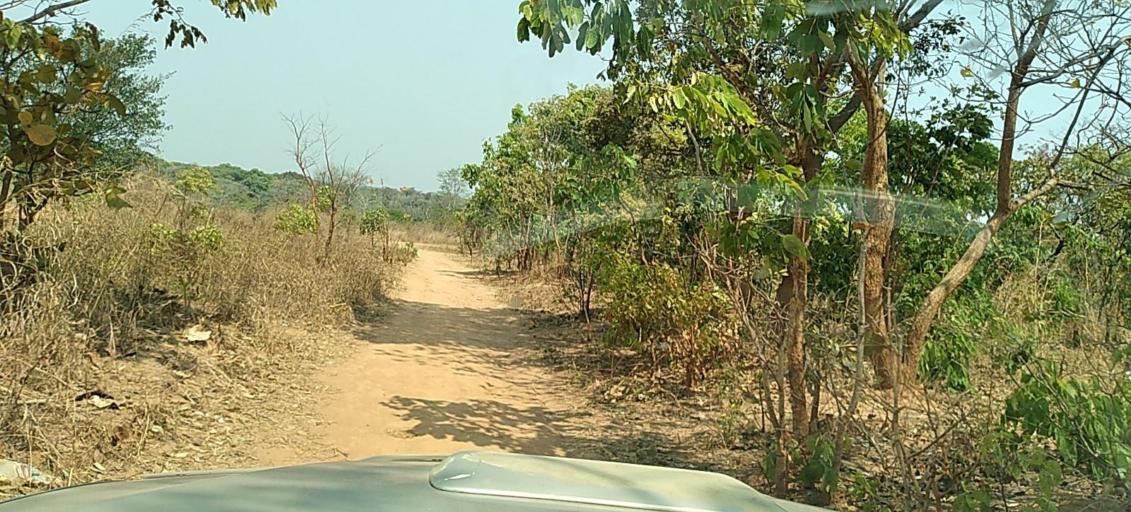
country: ZM
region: North-Western
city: Kasempa
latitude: -13.7105
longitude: 26.3386
